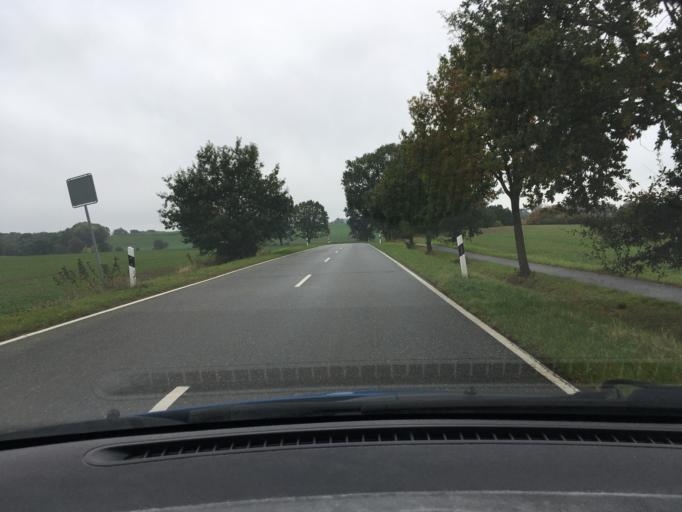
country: DE
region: Schleswig-Holstein
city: Bosdorf
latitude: 54.1304
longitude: 10.4782
